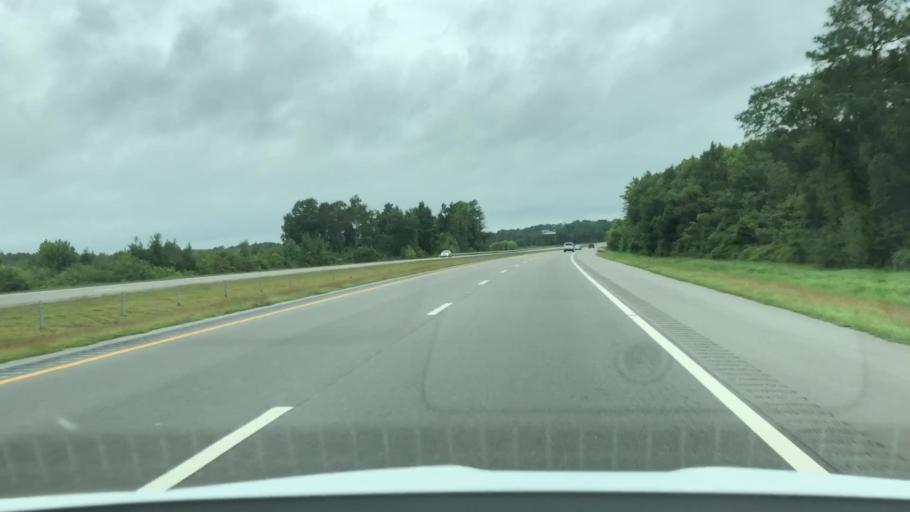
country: US
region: North Carolina
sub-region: Lenoir County
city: La Grange
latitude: 35.3278
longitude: -77.8406
